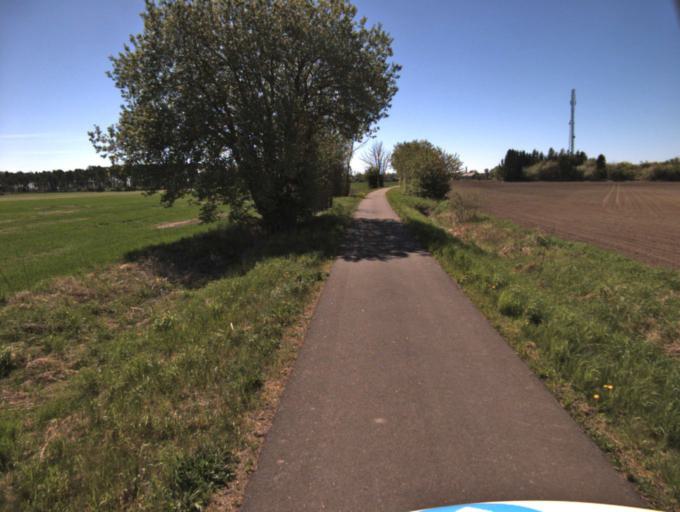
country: SE
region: Skane
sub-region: Kristianstads Kommun
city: Norra Asum
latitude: 55.9566
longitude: 14.1575
